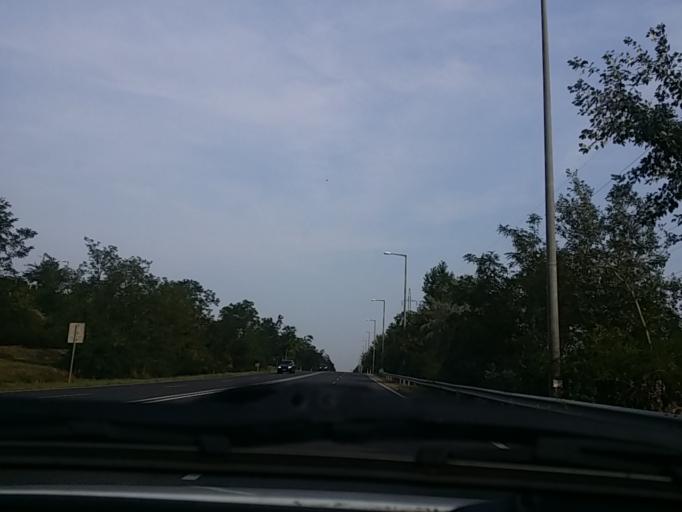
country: HU
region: Pest
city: Toeroekbalint
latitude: 47.4642
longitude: 18.8856
